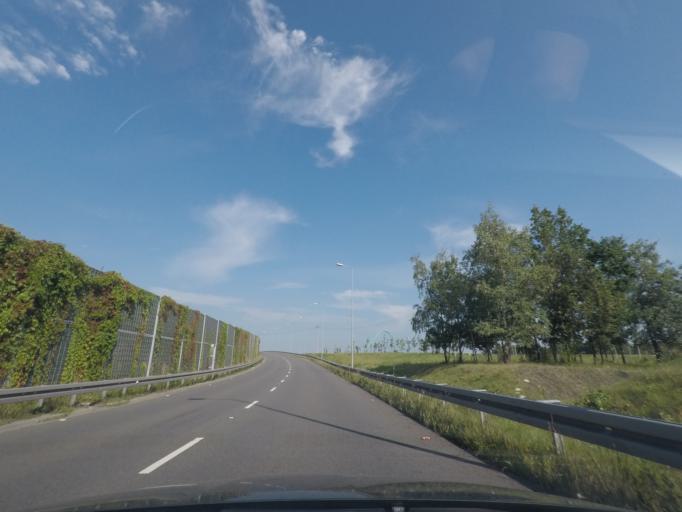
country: PL
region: Silesian Voivodeship
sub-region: Powiat wodzislawski
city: Mszana
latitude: 49.9586
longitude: 18.5156
